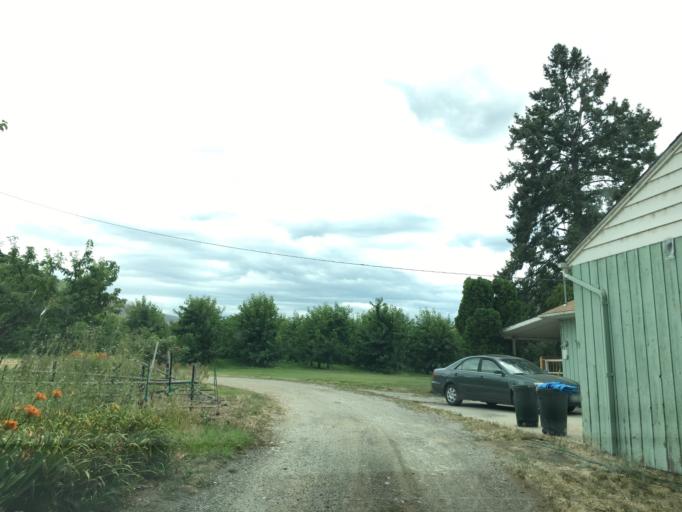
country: US
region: Washington
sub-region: Chelan County
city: Entiat
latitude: 47.6267
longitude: -120.2285
